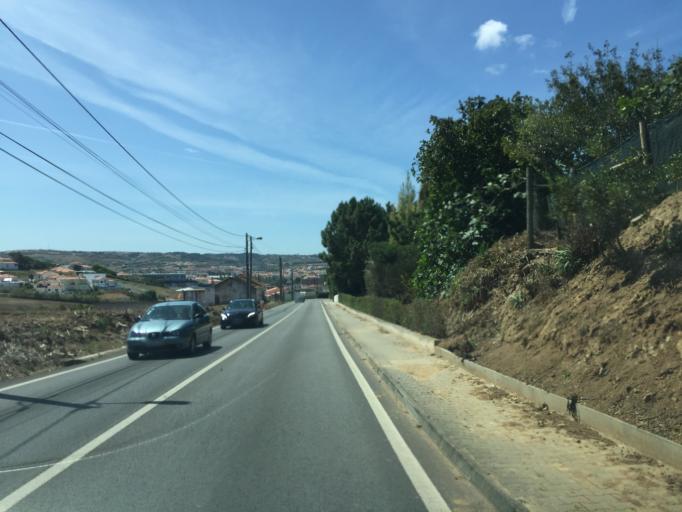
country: PT
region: Lisbon
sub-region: Lourinha
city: Lourinha
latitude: 39.2553
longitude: -9.3126
